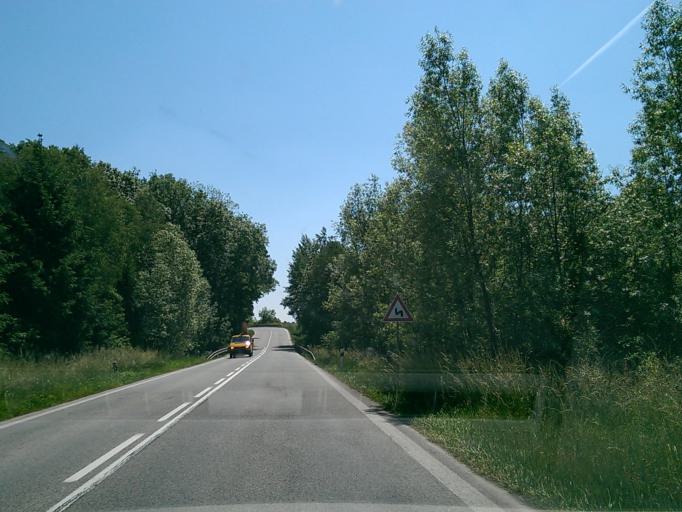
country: CZ
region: Liberecky
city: Rovensko pod Troskami
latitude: 50.5335
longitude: 15.2356
